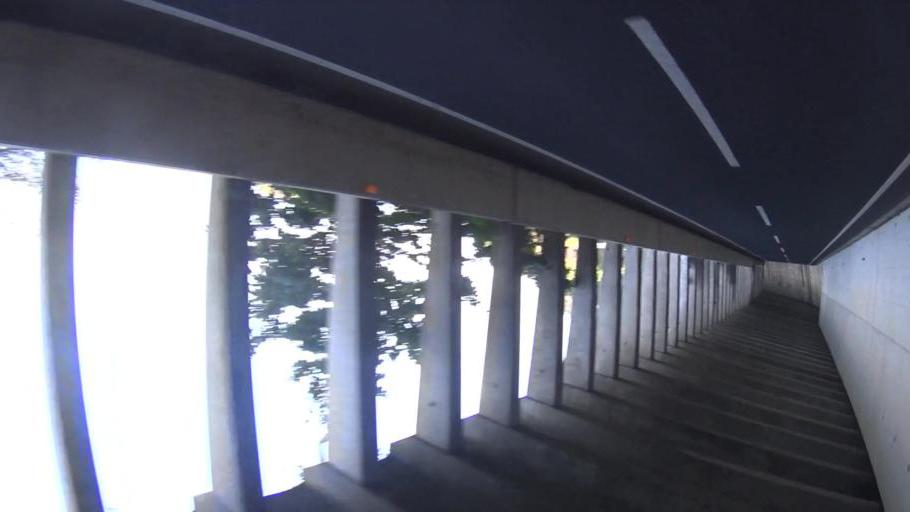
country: JP
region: Kyoto
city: Miyazu
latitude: 35.7622
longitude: 135.2392
